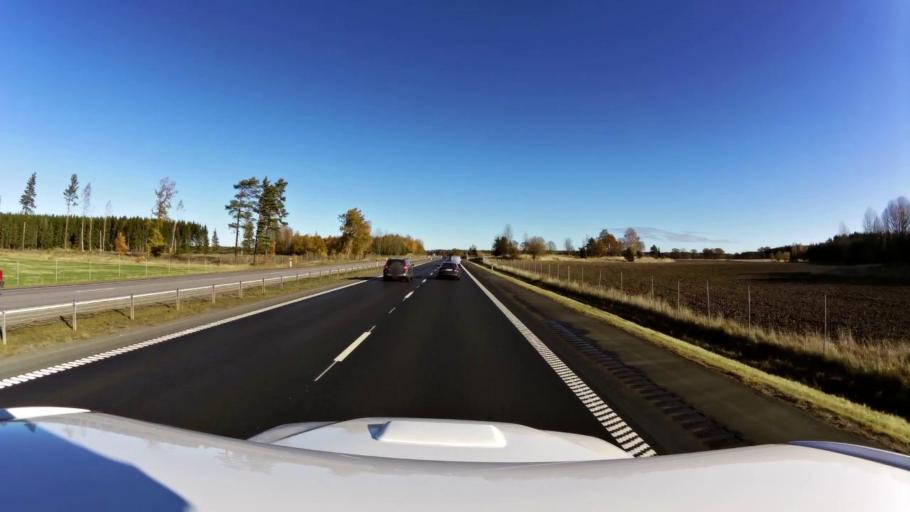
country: SE
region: OEstergoetland
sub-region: Linkopings Kommun
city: Vikingstad
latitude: 58.4071
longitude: 15.4526
